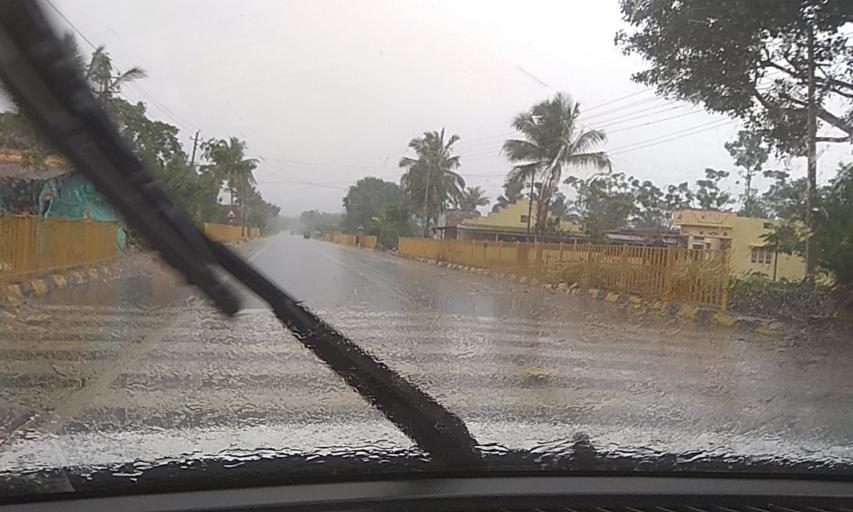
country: IN
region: Karnataka
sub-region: Mandya
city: Maddur
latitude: 12.7176
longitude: 77.0572
